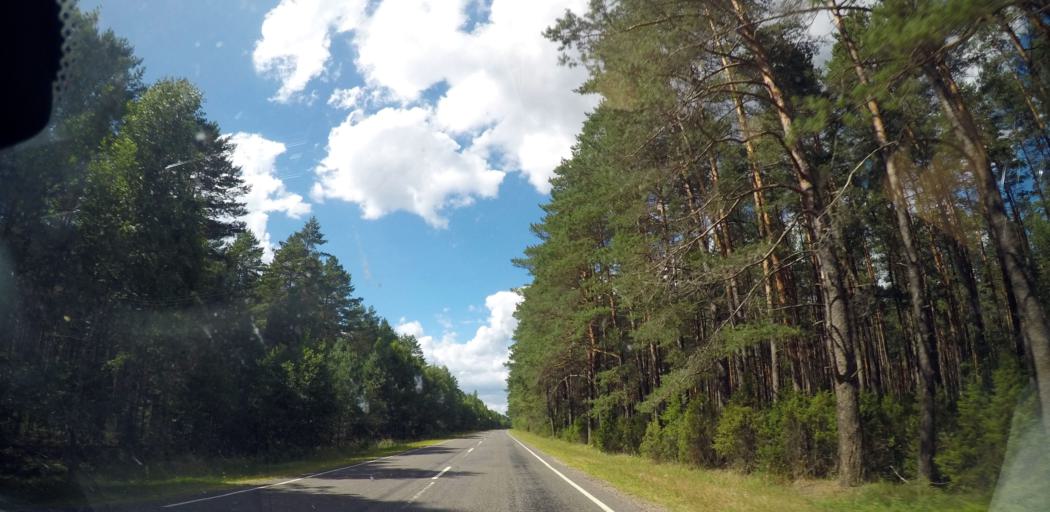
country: BY
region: Grodnenskaya
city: Skidal'
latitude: 53.8501
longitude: 24.1970
